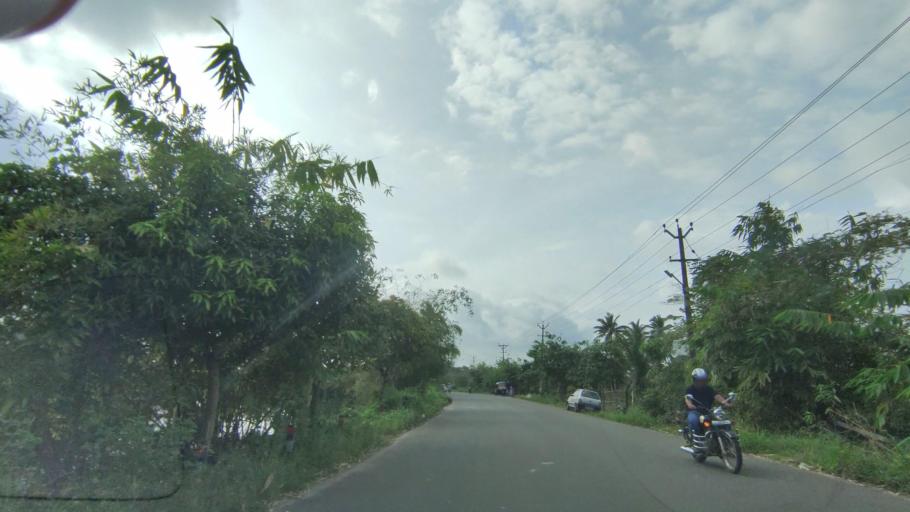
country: IN
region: Kerala
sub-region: Kottayam
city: Kottayam
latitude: 9.5693
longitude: 76.5030
